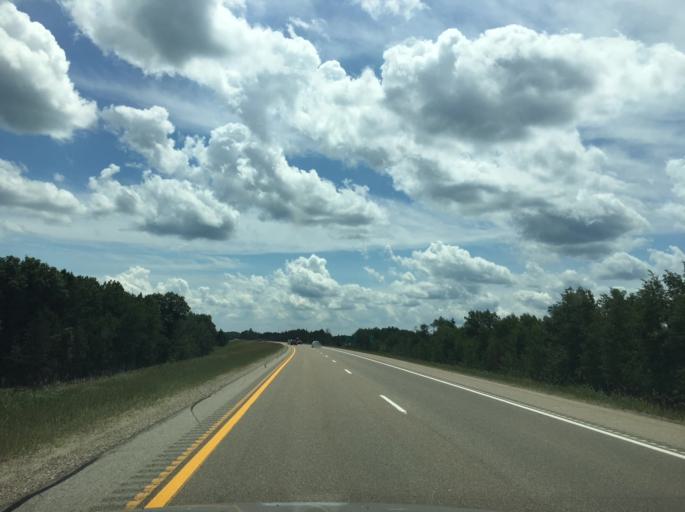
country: US
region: Michigan
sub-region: Crawford County
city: Grayling
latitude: 44.5770
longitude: -84.7100
